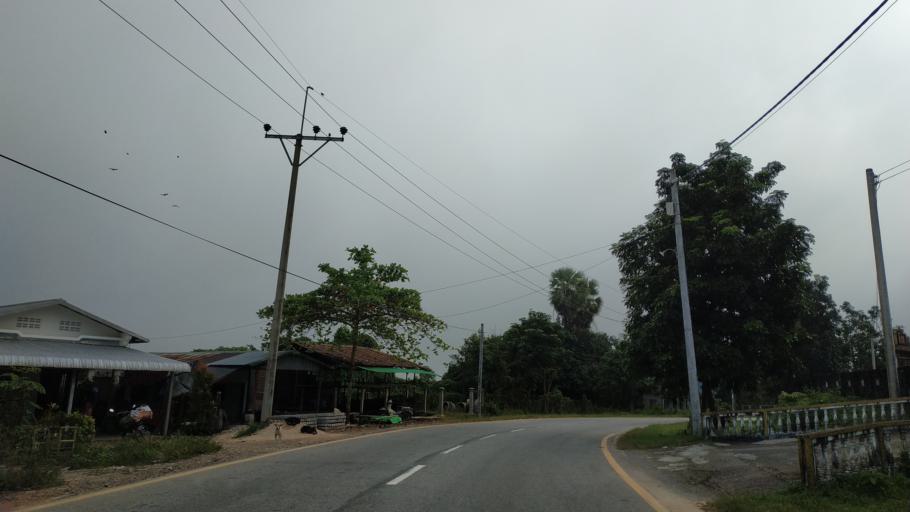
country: MM
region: Tanintharyi
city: Dawei
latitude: 14.1136
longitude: 98.1973
